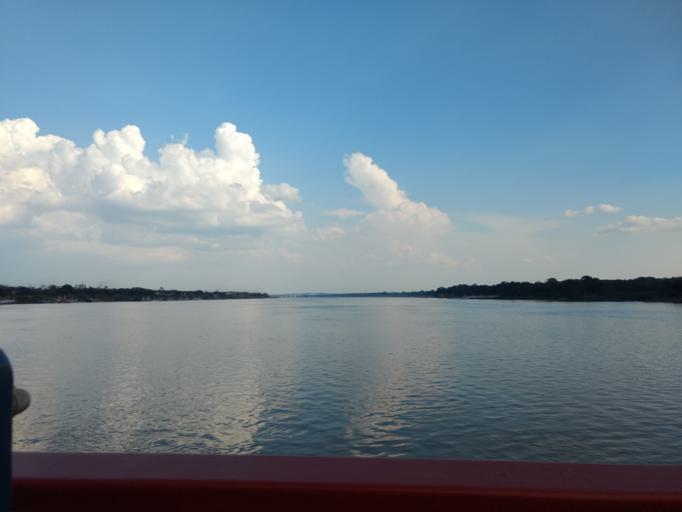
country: BR
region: Rondonia
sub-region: Porto Velho
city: Porto Velho
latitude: -8.6884
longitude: -63.9214
